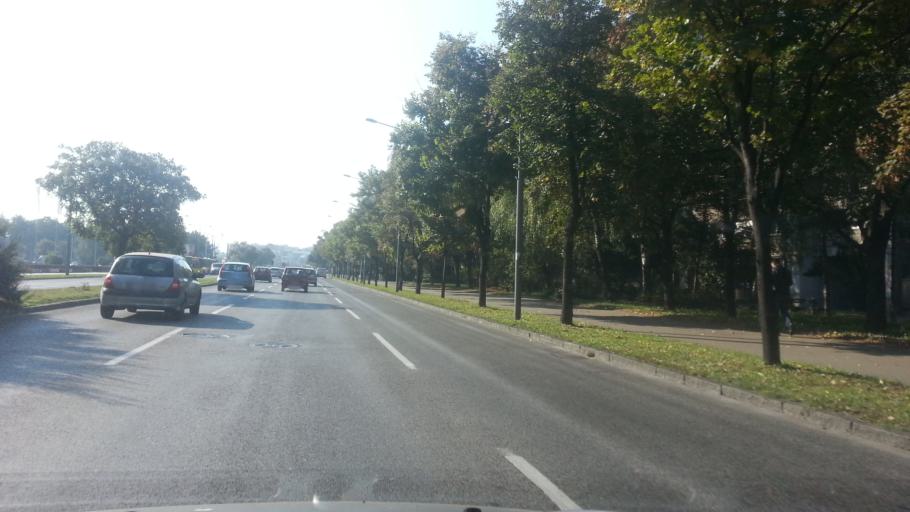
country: RS
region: Central Serbia
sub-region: Belgrade
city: Zemun
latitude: 44.8301
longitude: 20.4191
